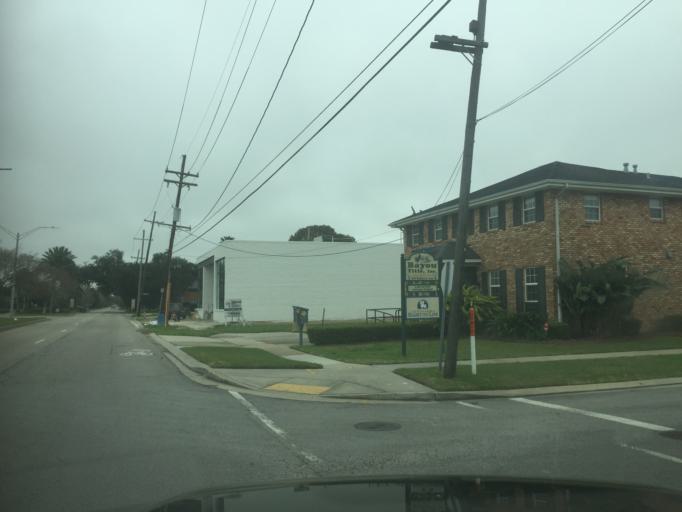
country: US
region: Louisiana
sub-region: Jefferson Parish
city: Metairie
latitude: 30.0200
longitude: -90.1126
